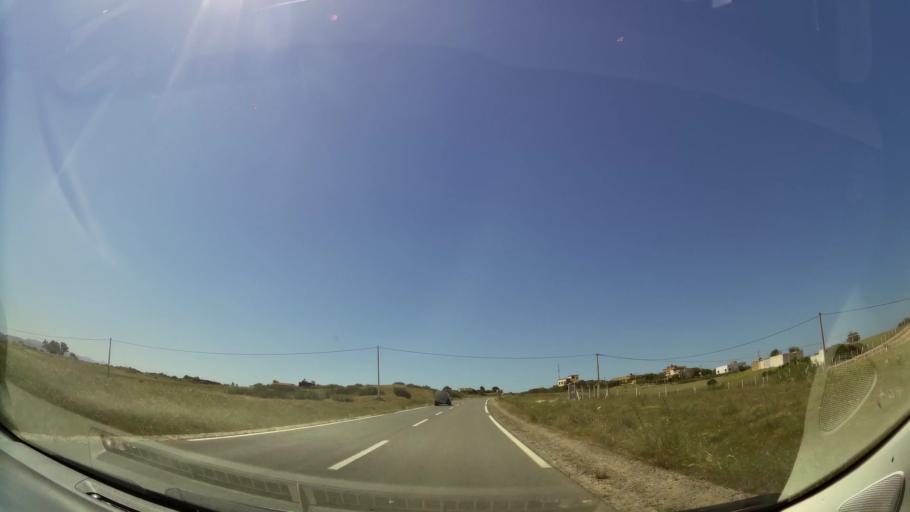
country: MA
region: Oriental
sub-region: Berkane-Taourirt
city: Madagh
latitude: 35.1209
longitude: -2.3790
